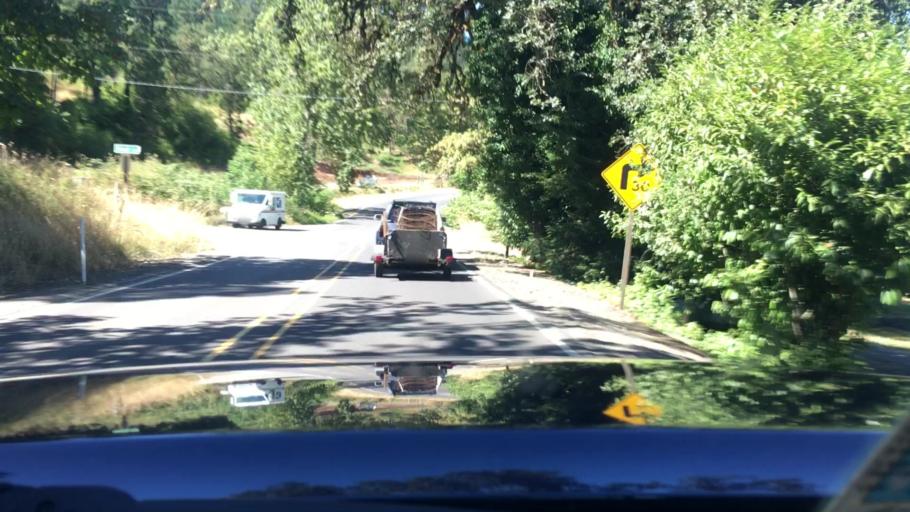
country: US
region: Oregon
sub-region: Lane County
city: Cottage Grove
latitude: 43.8201
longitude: -123.0465
